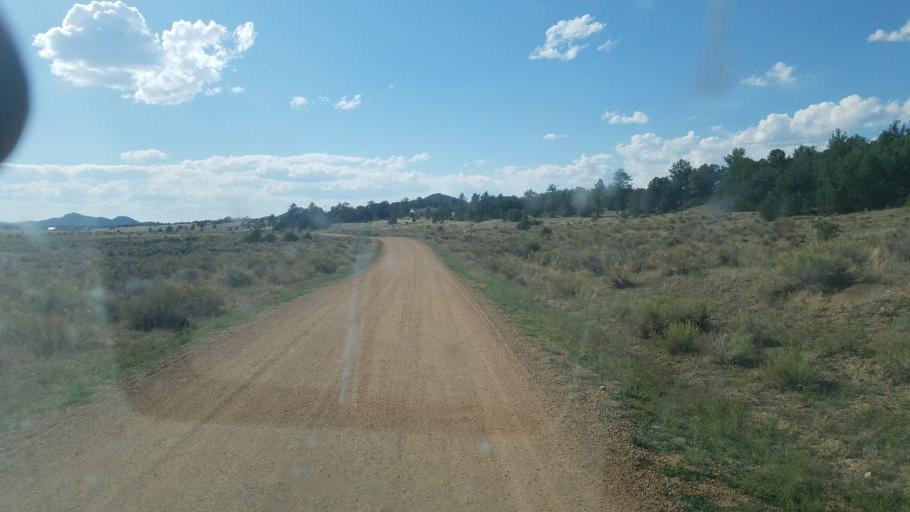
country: US
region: Colorado
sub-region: Custer County
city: Westcliffe
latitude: 38.2823
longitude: -105.4716
